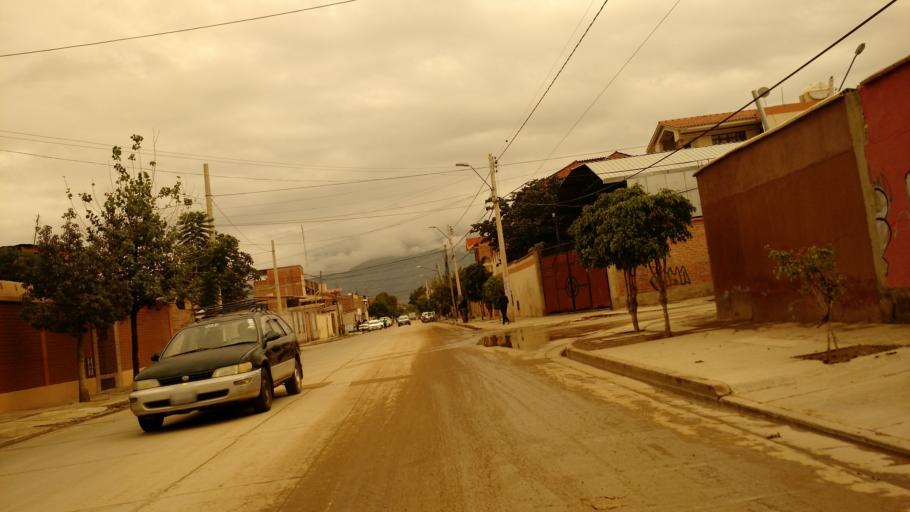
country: BO
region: Cochabamba
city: Cochabamba
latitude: -17.4361
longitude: -66.1550
